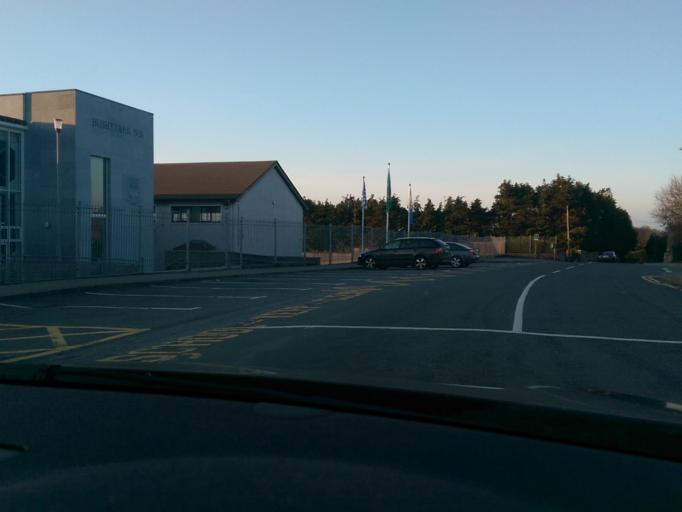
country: IE
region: Connaught
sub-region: County Galway
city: Gaillimh
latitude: 53.2897
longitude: -9.0827
